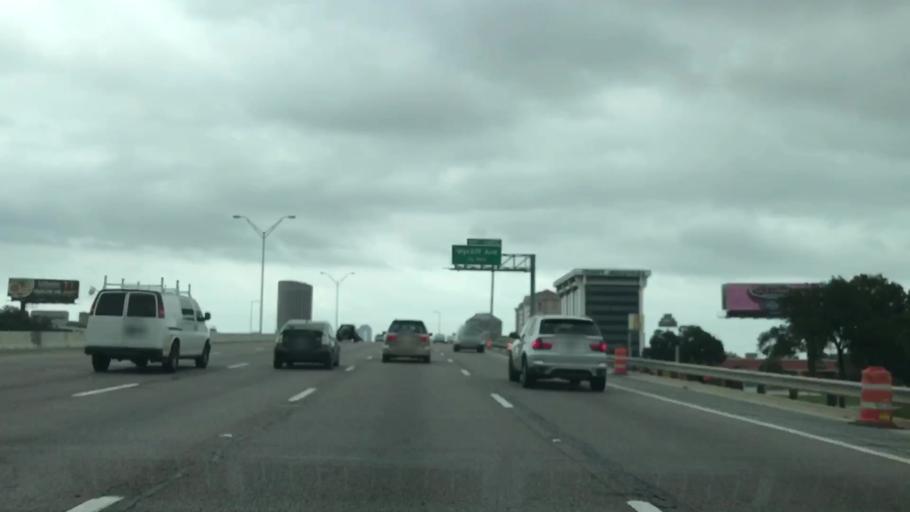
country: US
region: Texas
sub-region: Dallas County
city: Dallas
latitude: 32.8077
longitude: -96.8429
